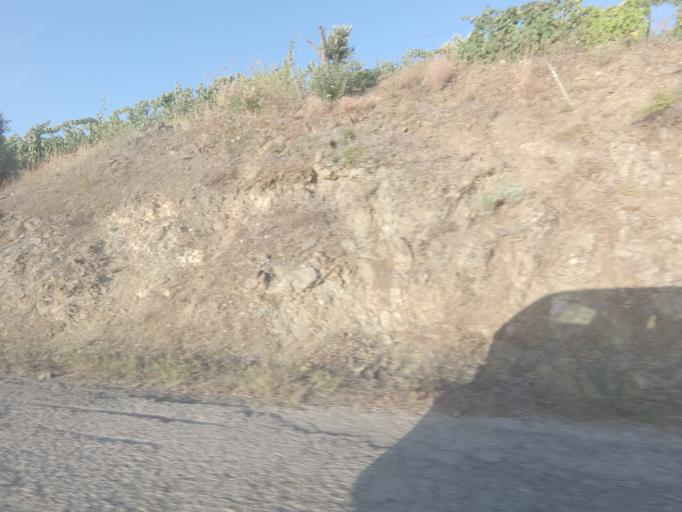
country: PT
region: Viseu
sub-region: Armamar
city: Armamar
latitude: 41.1221
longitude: -7.6736
